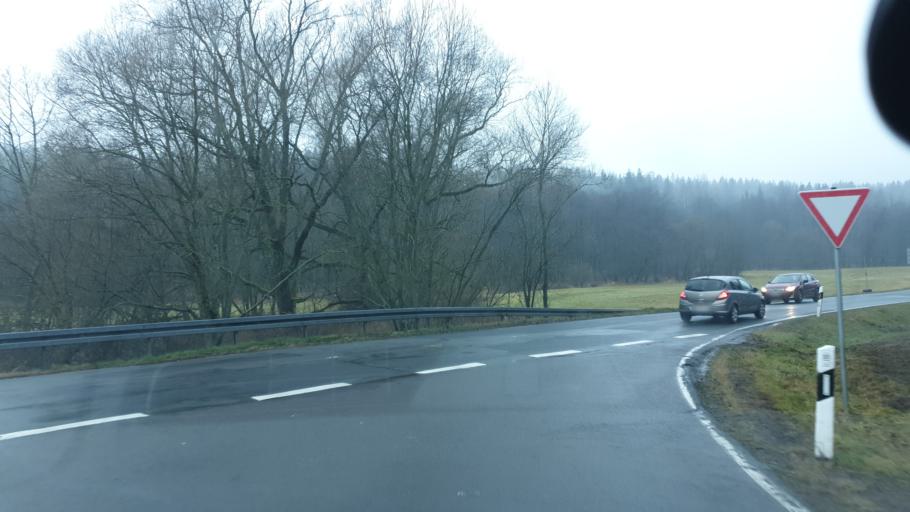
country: DE
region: Saxony
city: Seiffen
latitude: 50.6273
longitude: 13.4101
